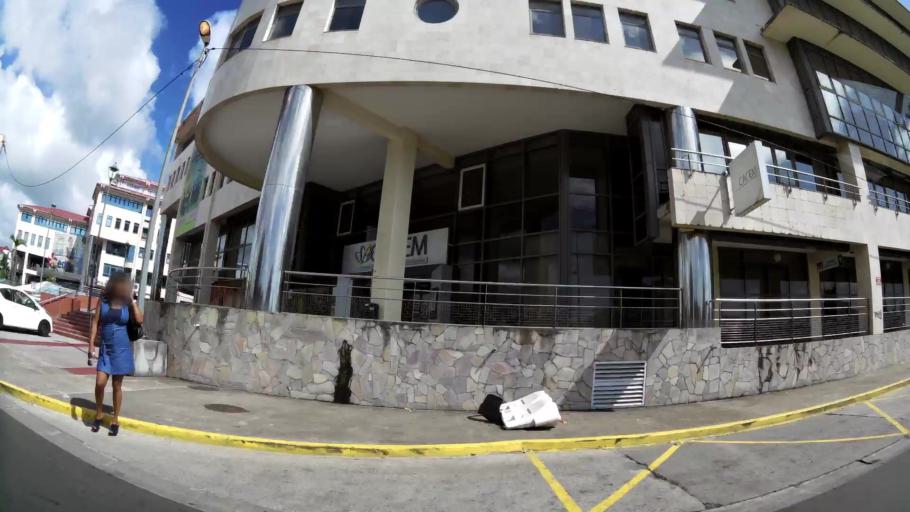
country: MQ
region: Martinique
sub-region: Martinique
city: Fort-de-France
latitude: 14.6043
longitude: -61.0636
